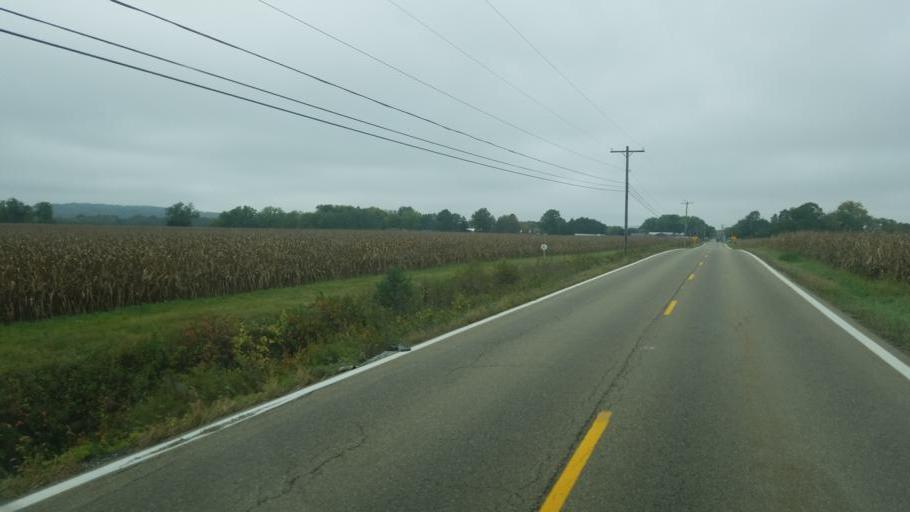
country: US
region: Ohio
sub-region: Stark County
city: Beach City
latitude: 40.6467
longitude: -81.5418
